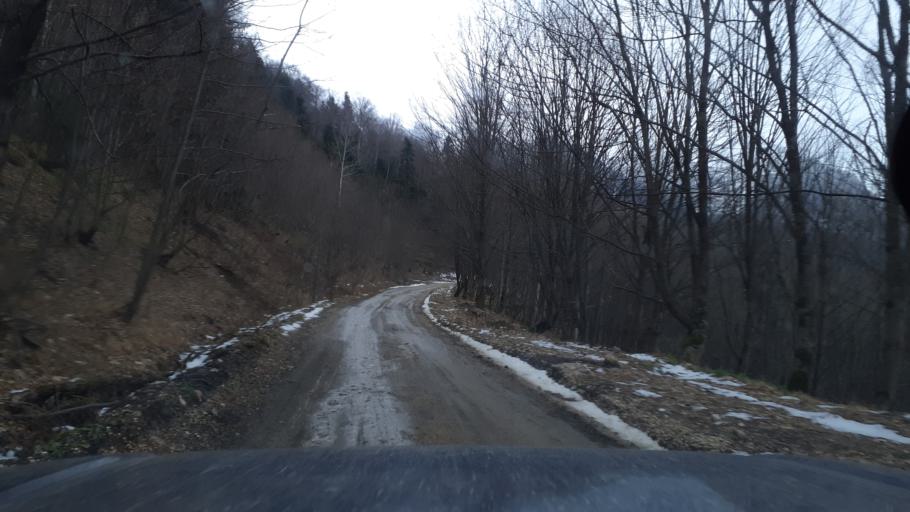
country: RU
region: Krasnodarskiy
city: Neftegorsk
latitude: 44.0788
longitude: 39.7978
